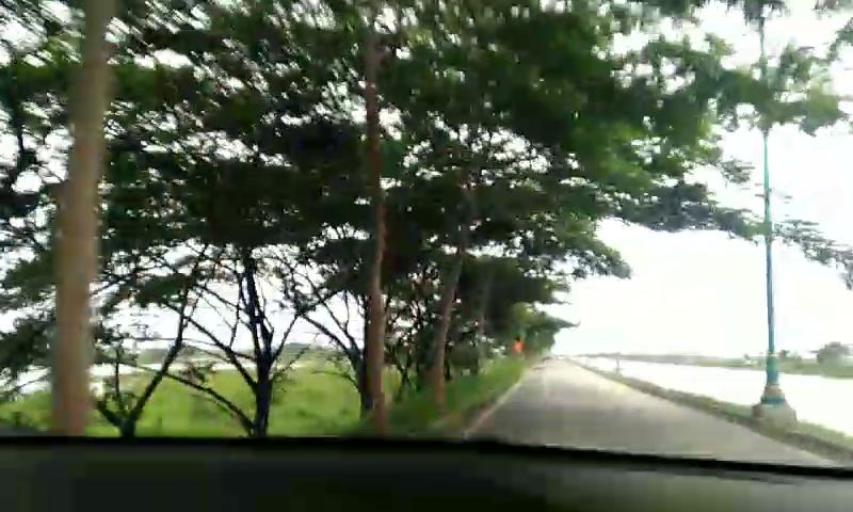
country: ID
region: West Java
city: Bekasi
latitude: -6.1249
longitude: 106.9692
